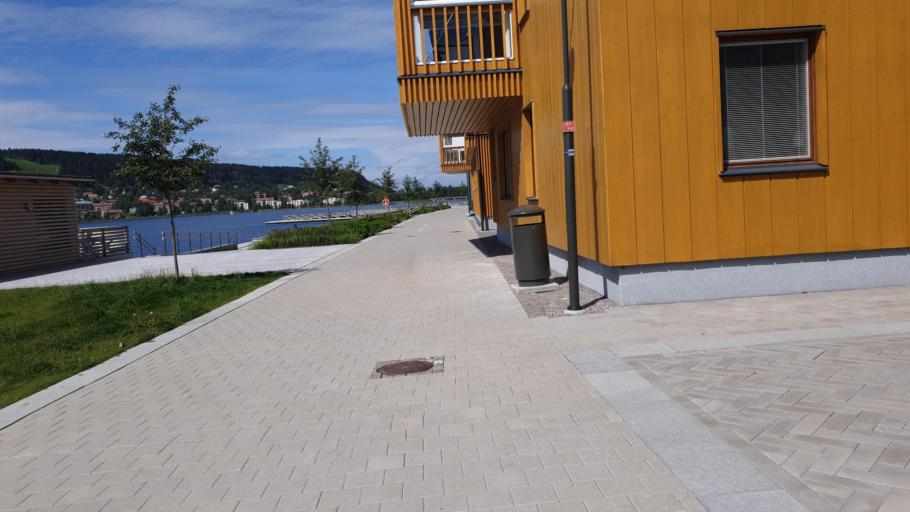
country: SE
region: Jaemtland
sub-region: OEstersunds Kommun
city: Ostersund
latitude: 63.1726
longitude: 14.6316
